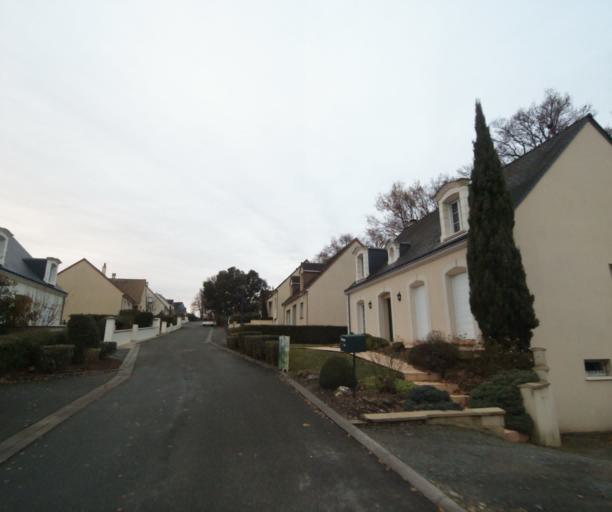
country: FR
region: Pays de la Loire
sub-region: Departement de la Sarthe
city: Coulaines
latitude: 48.0240
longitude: 0.2139
